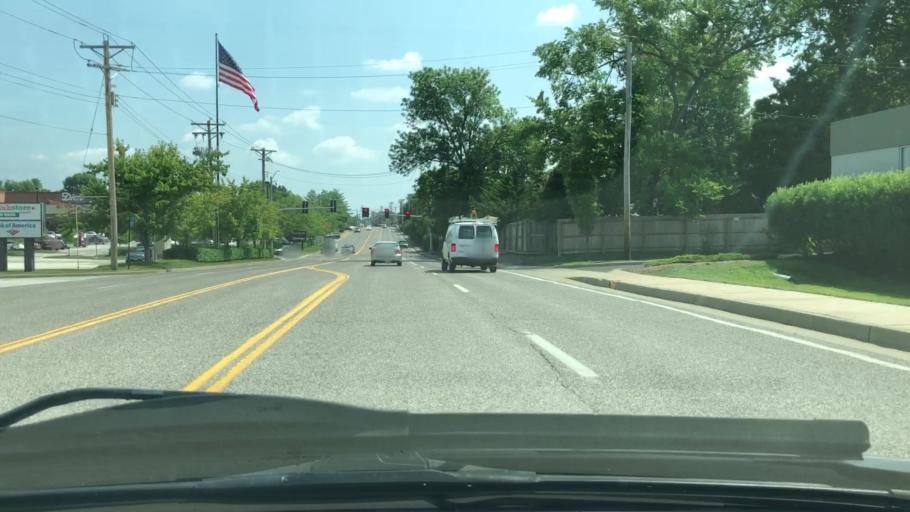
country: US
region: Missouri
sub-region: Saint Louis County
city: Warson Woods
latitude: 38.6036
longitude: -90.3831
